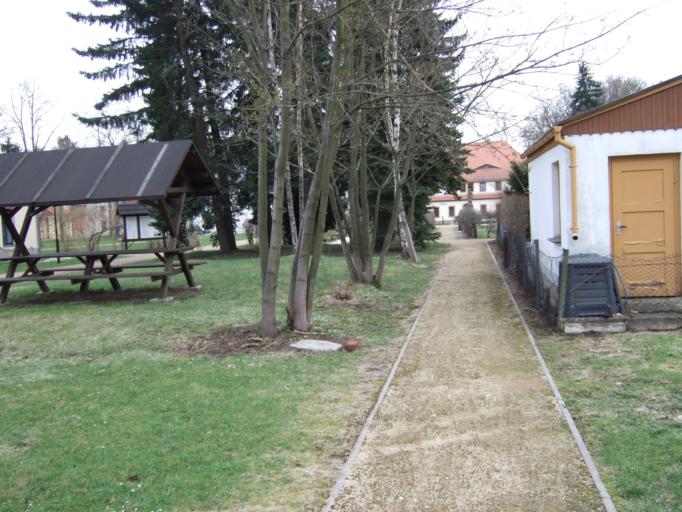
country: DE
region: Saxony
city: Brand-Erbisdorf
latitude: 50.8709
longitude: 13.3374
